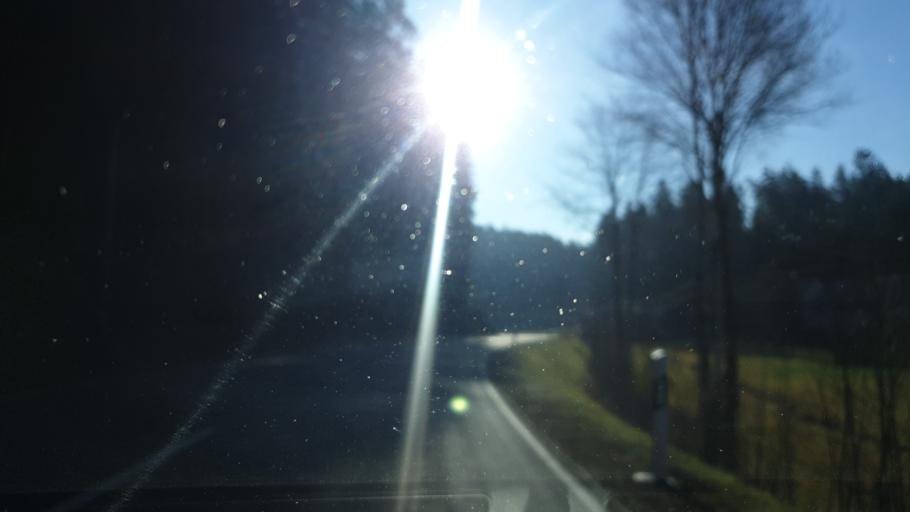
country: DE
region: Saxony
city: Bad Brambach
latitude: 50.2562
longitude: 12.3034
